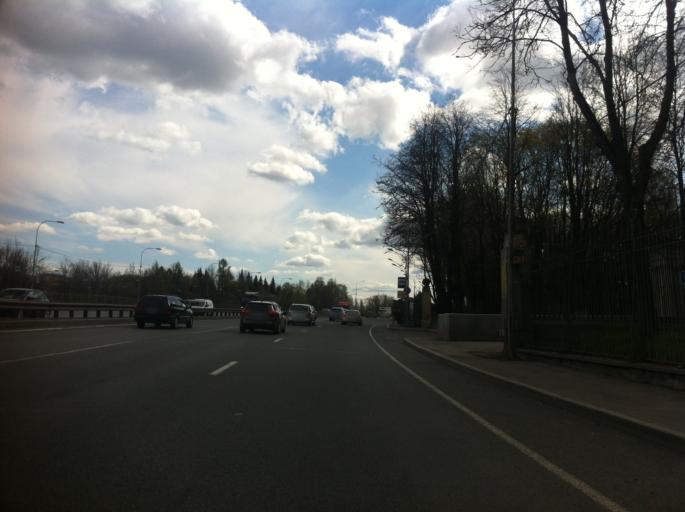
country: RU
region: St.-Petersburg
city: Aleksandrovskaya
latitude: 59.7712
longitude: 30.3323
